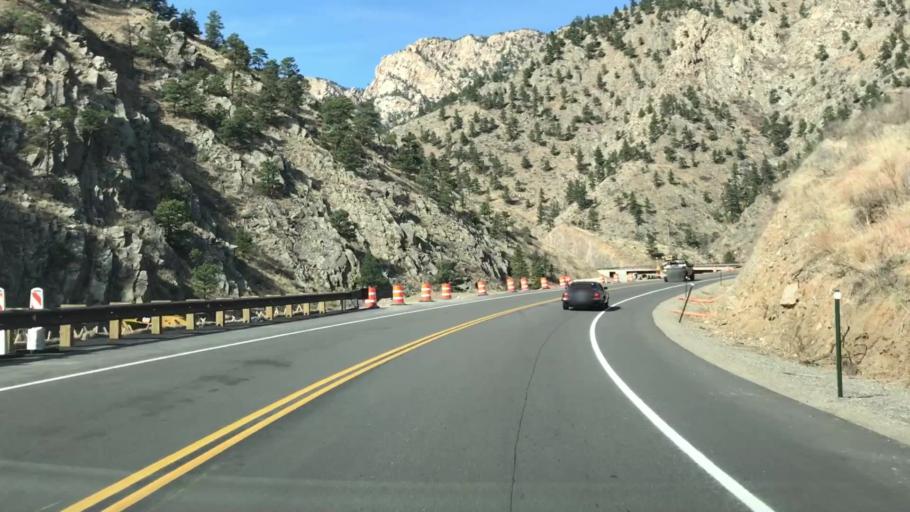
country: US
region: Colorado
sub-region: Boulder County
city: Lyons
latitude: 40.4245
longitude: -105.2924
